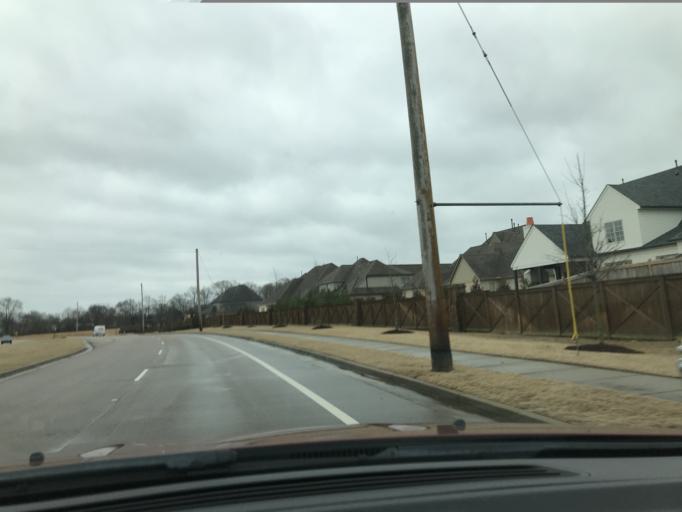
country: US
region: Tennessee
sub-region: Shelby County
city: Collierville
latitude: 35.0873
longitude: -89.7059
